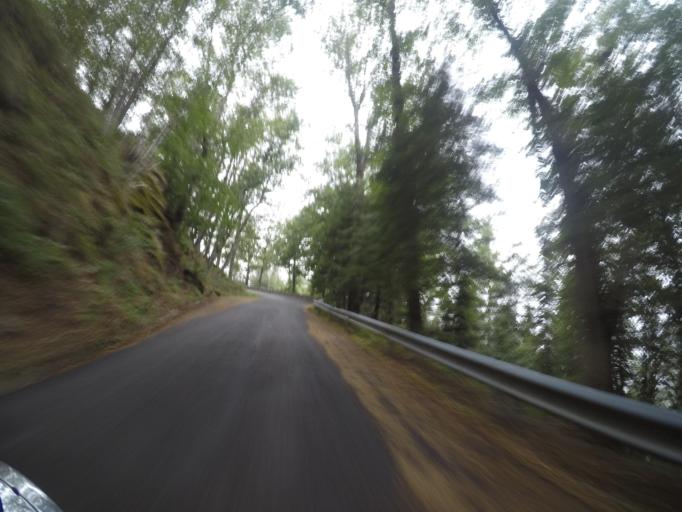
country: IT
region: Tuscany
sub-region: Provincia di Massa-Carrara
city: Carrara
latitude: 44.1153
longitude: 10.1173
